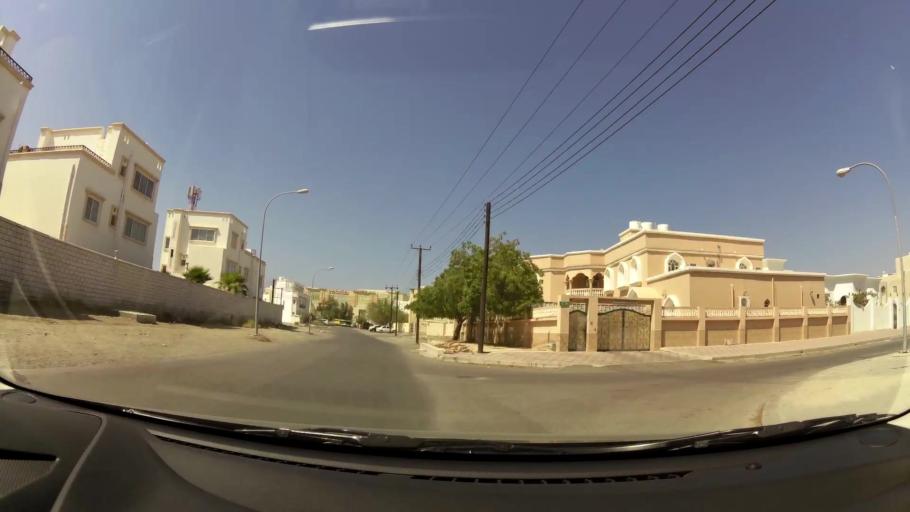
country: OM
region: Muhafazat Masqat
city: As Sib al Jadidah
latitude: 23.6383
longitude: 58.2220
